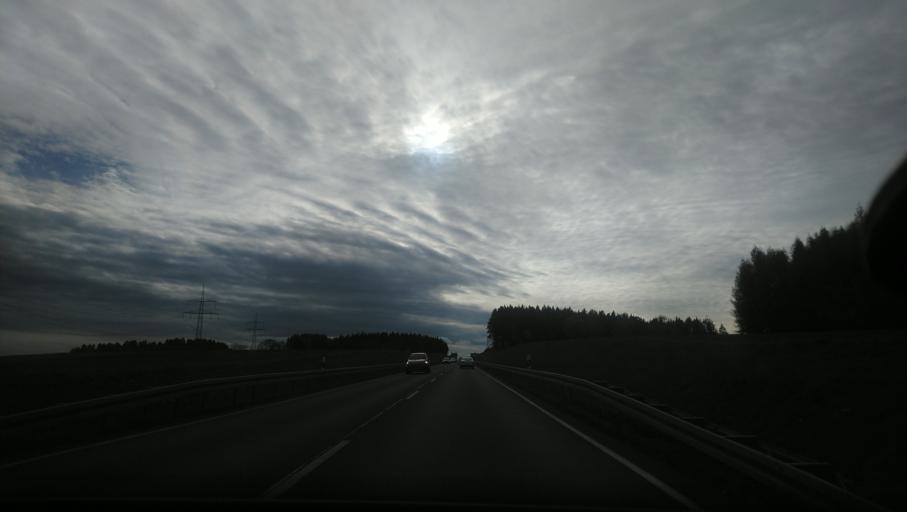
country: DE
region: Saxony
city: Stollberg
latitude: 50.6811
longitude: 12.8035
